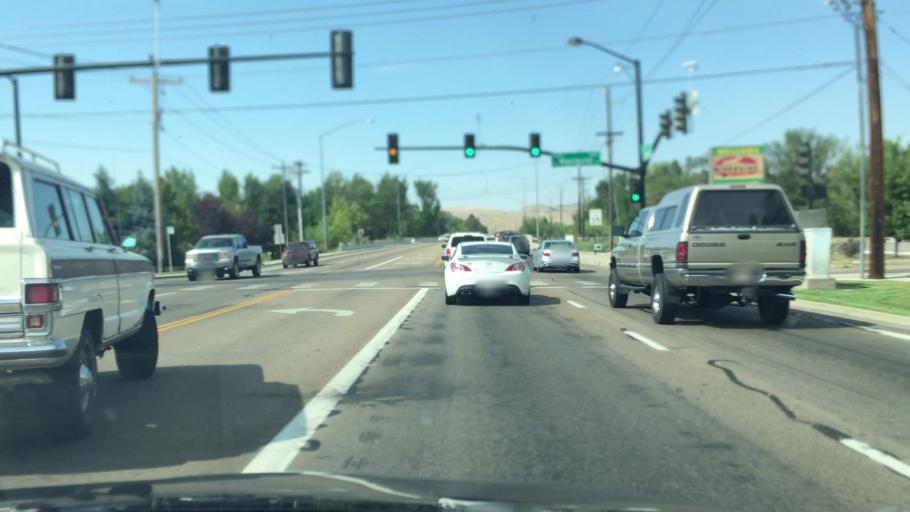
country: US
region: Idaho
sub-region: Ada County
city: Garden City
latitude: 43.6590
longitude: -116.2797
